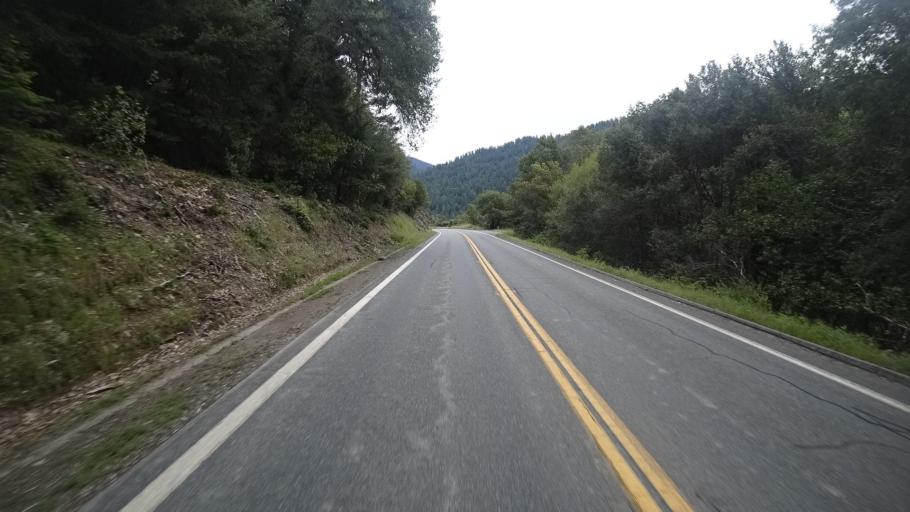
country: US
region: California
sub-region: Humboldt County
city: Willow Creek
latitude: 41.2775
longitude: -123.5997
